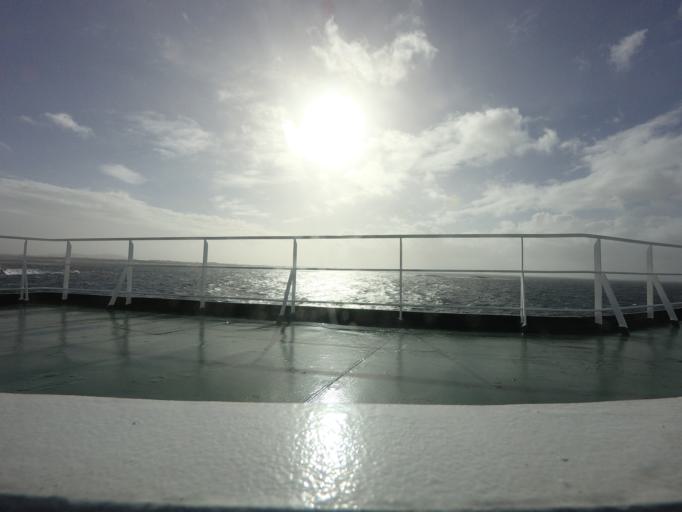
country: NO
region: Sogn og Fjordane
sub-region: Solund
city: Hardbakke
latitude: 60.9465
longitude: 4.7560
